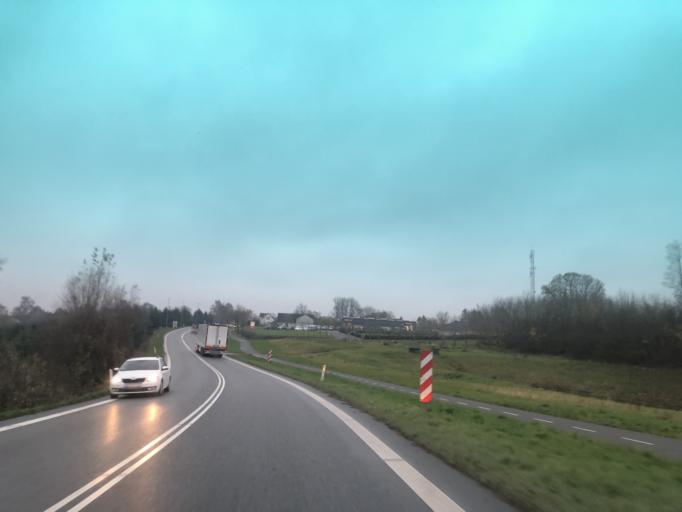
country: DK
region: South Denmark
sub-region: Nyborg Kommune
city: Ullerslev
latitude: 55.2667
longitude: 10.6752
